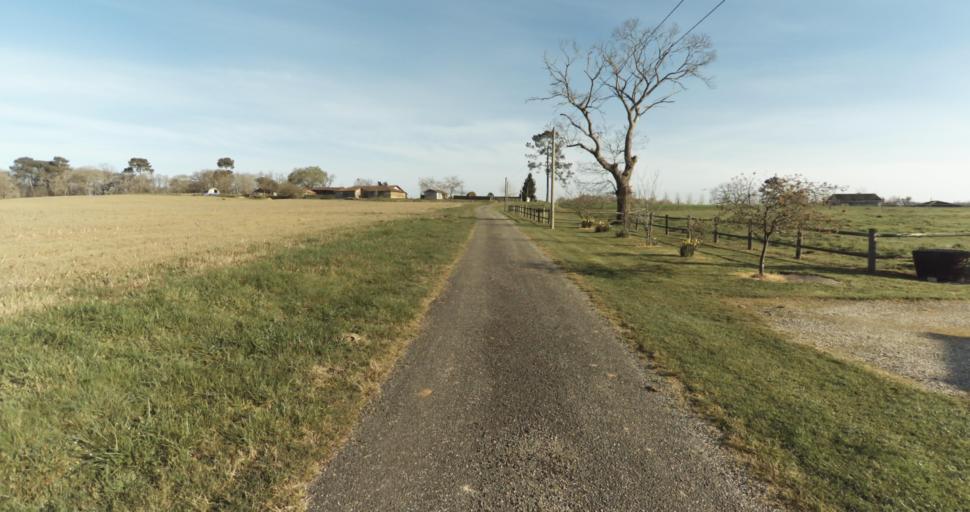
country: FR
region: Midi-Pyrenees
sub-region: Departement du Gers
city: Cazaubon
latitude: 43.9777
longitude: -0.1288
